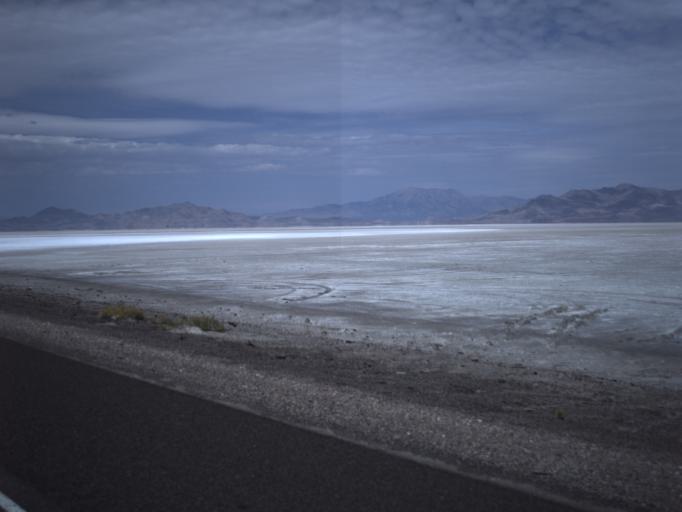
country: US
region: Utah
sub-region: Tooele County
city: Wendover
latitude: 40.7358
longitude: -113.6762
